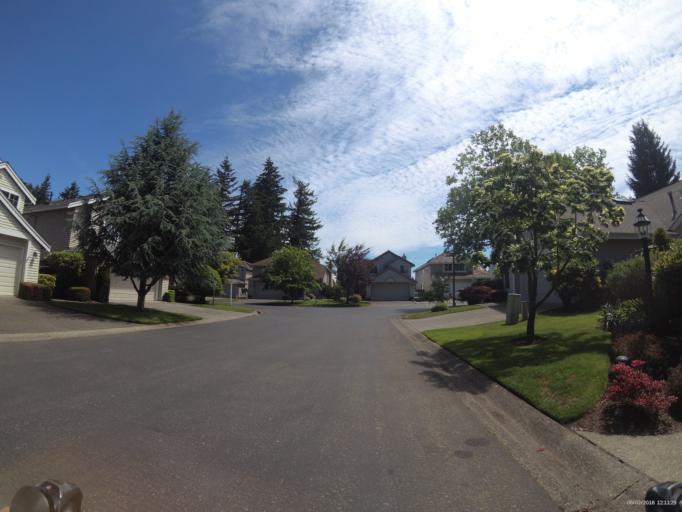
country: US
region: Washington
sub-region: Pierce County
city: University Place
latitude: 47.2001
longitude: -122.5484
